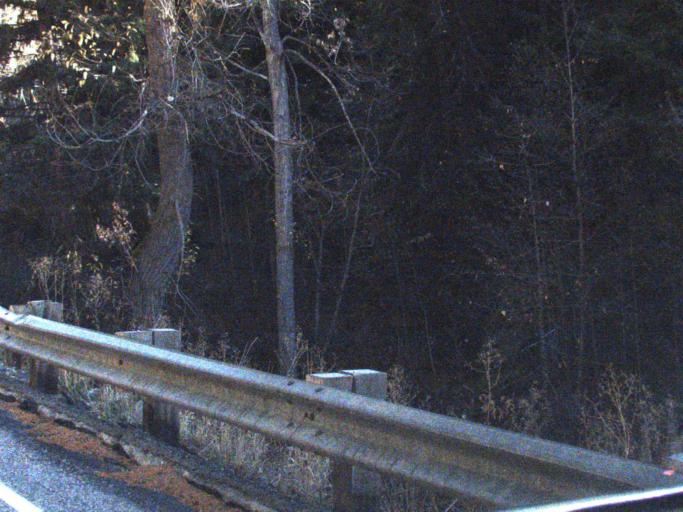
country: US
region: Washington
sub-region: Ferry County
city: Republic
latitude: 48.5972
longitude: -118.6294
